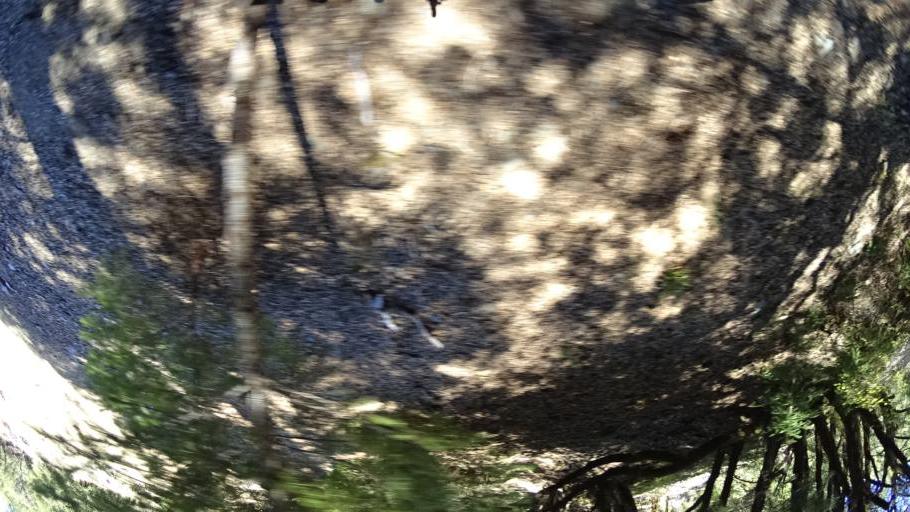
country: US
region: California
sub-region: Siskiyou County
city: Happy Camp
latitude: 41.3082
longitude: -123.1670
